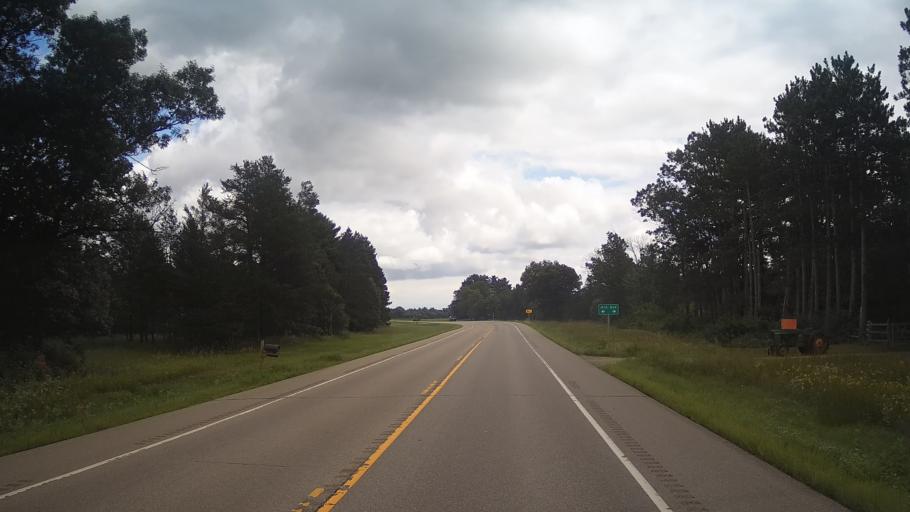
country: US
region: Wisconsin
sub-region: Adams County
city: Friendship
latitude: 44.0223
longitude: -89.6616
